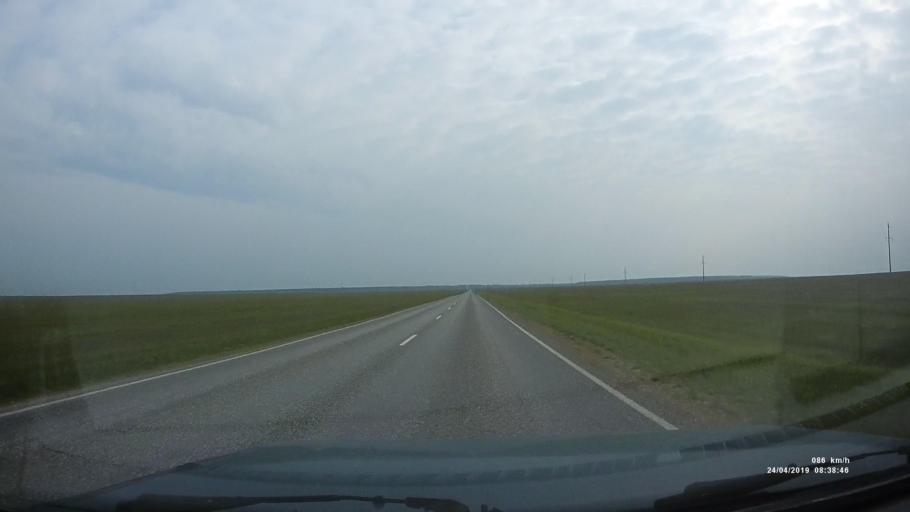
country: RU
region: Kalmykiya
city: Arshan'
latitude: 46.2171
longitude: 43.9727
